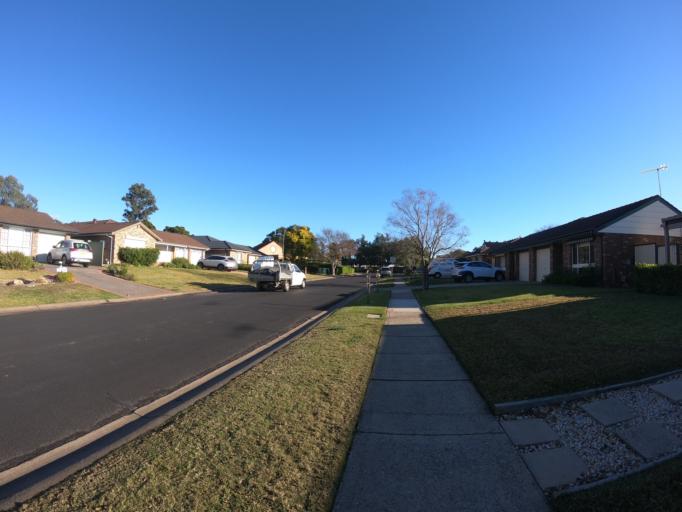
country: AU
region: New South Wales
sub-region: Hawkesbury
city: South Windsor
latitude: -33.6408
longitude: 150.7955
